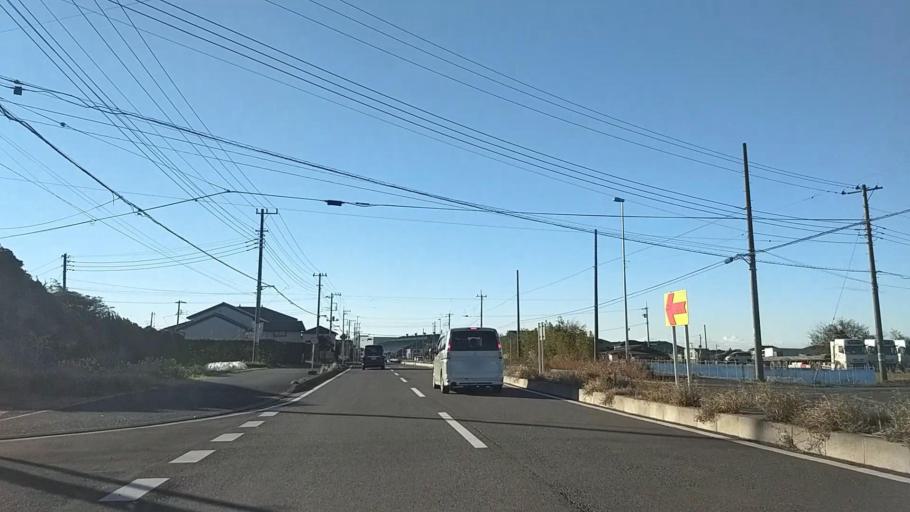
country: JP
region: Chiba
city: Kisarazu
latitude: 35.4094
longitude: 139.9185
